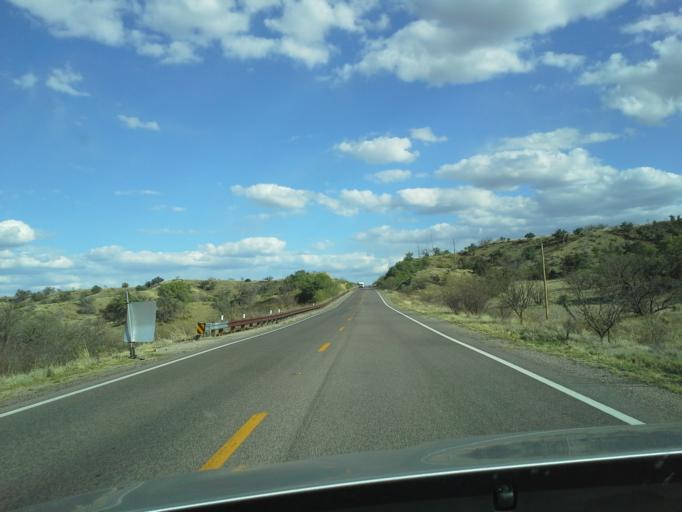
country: US
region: Arizona
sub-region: Pima County
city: Corona de Tucson
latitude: 31.7799
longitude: -110.6916
